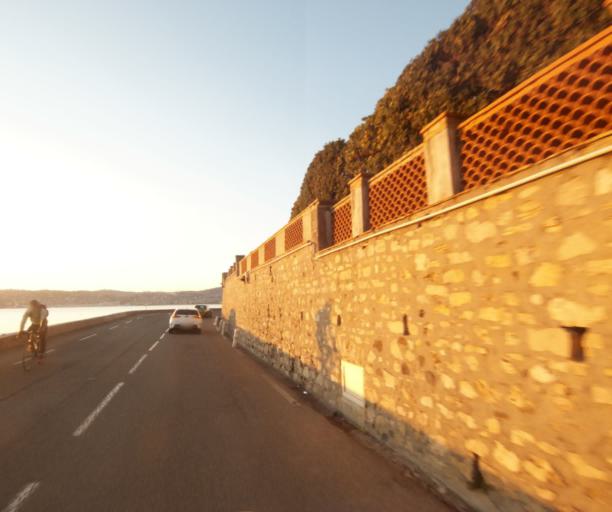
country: FR
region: Provence-Alpes-Cote d'Azur
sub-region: Departement des Alpes-Maritimes
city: Antibes
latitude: 43.5551
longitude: 7.1218
